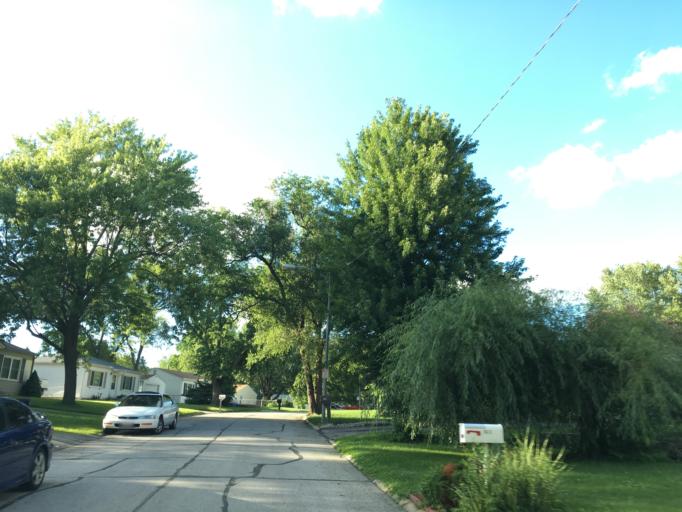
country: US
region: Nebraska
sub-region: Sarpy County
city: La Vista
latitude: 41.1837
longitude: -95.9741
